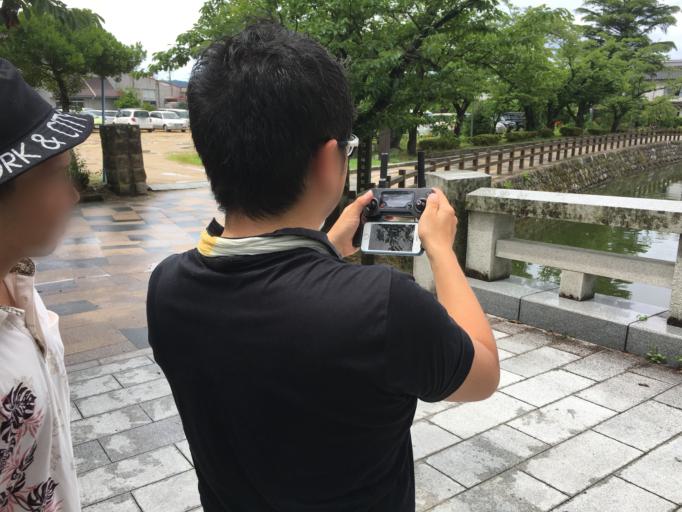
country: JP
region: Tottori
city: Tottori
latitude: 35.4598
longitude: 134.0639
